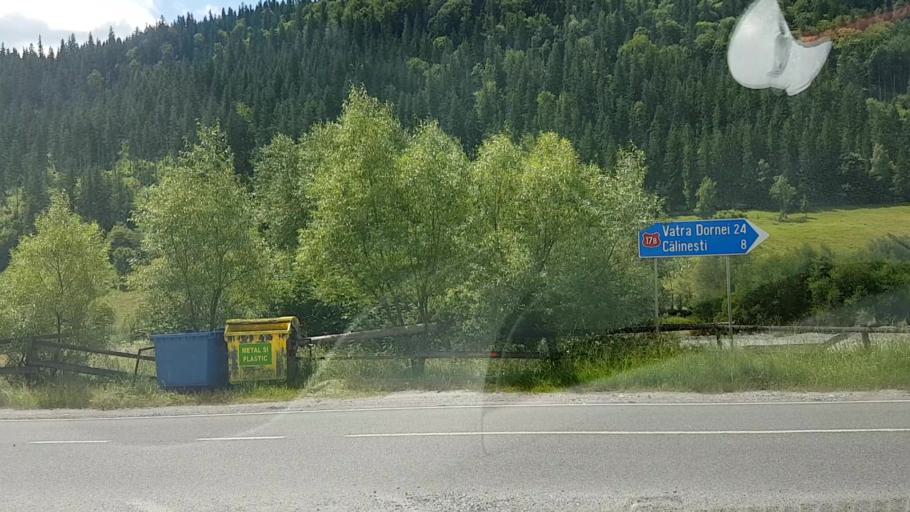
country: RO
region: Suceava
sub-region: Comuna Crucea
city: Crucea
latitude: 47.3962
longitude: 25.5635
